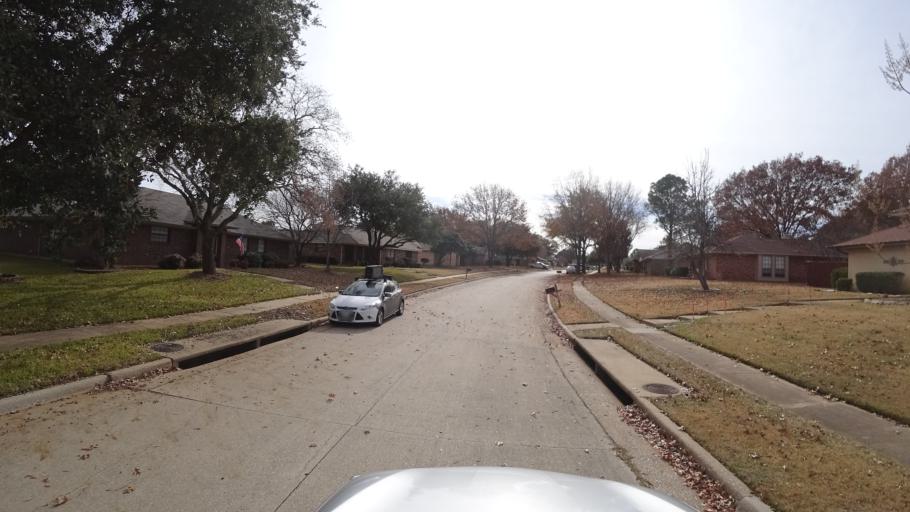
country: US
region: Texas
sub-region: Denton County
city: Highland Village
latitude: 33.0795
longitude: -97.0316
